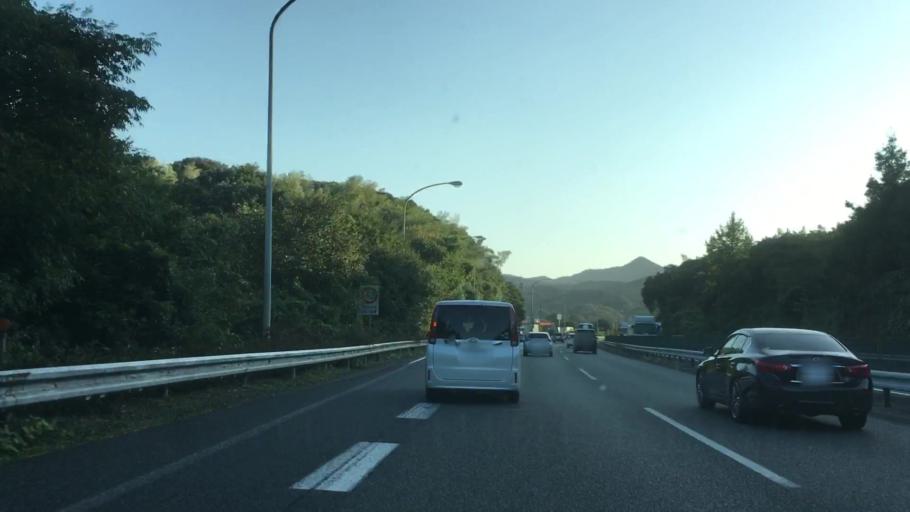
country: JP
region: Yamaguchi
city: Shimonoseki
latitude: 34.0532
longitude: 131.0061
